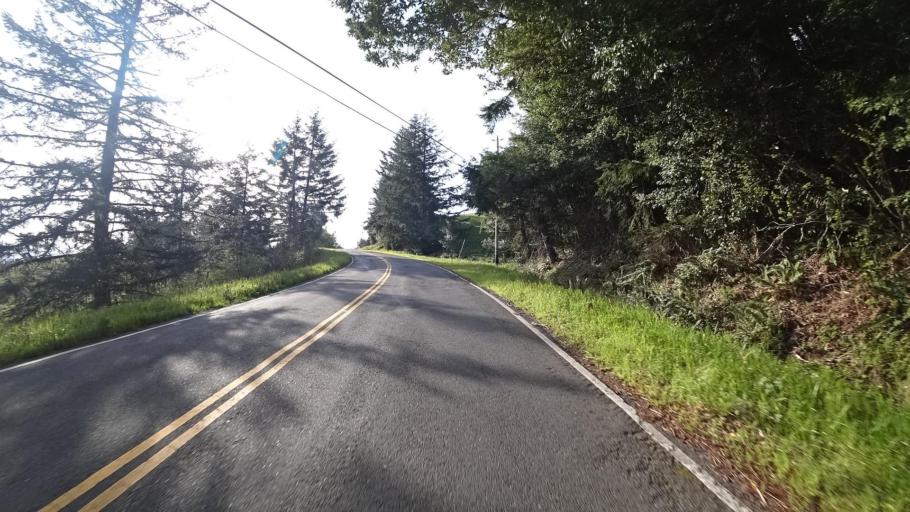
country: US
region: California
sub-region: Humboldt County
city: Blue Lake
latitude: 40.7392
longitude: -123.9514
